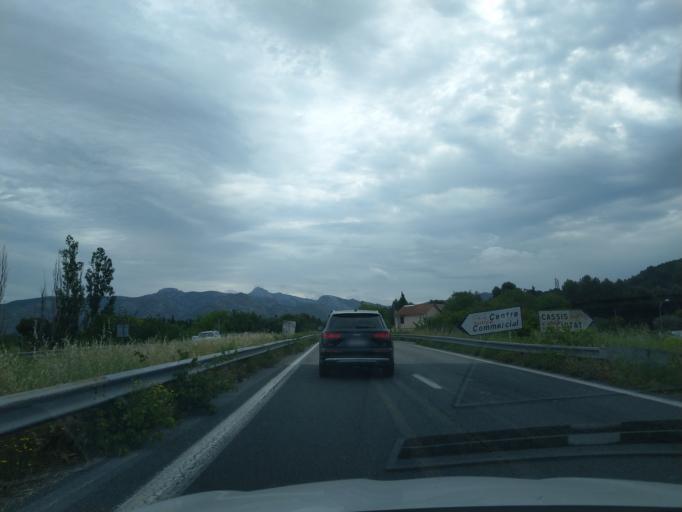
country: FR
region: Provence-Alpes-Cote d'Azur
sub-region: Departement des Bouches-du-Rhone
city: Aubagne
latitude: 43.2834
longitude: 5.5823
